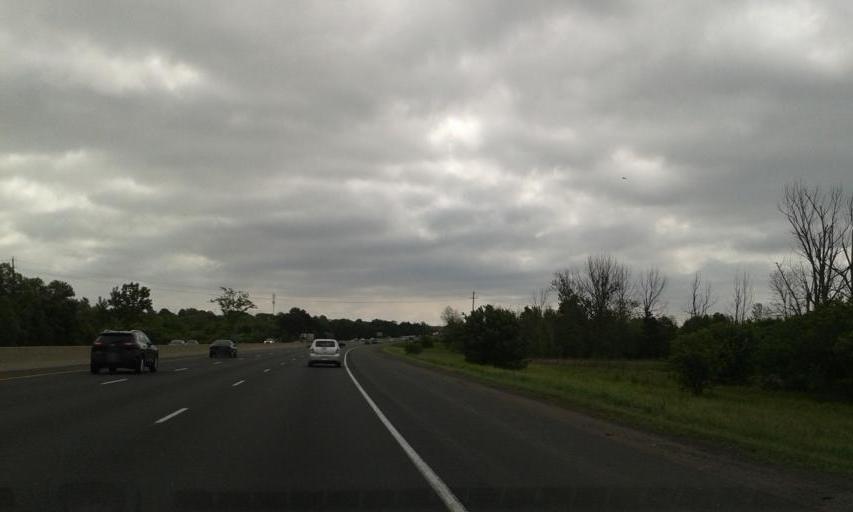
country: CA
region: Ontario
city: Oshawa
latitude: 43.8859
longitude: -78.8176
